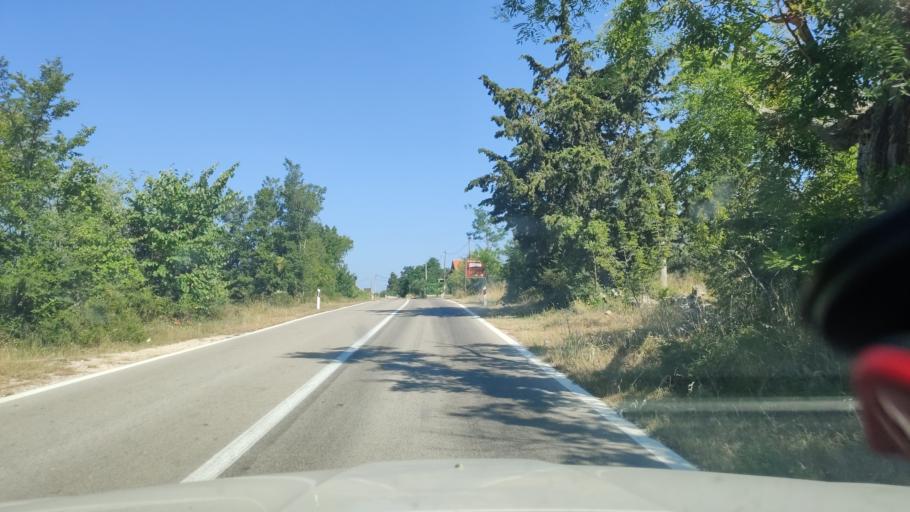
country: HR
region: Sibensko-Kniniska
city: Zaton
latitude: 43.9108
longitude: 15.8477
